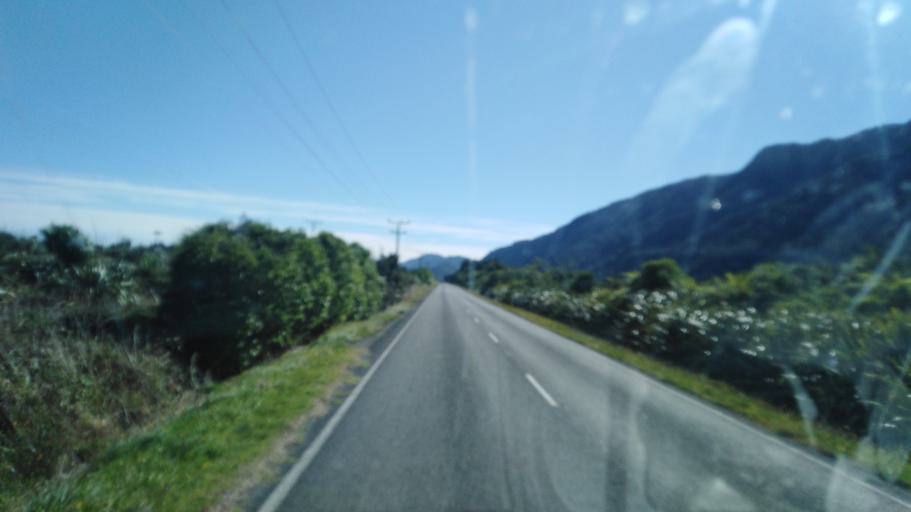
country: NZ
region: West Coast
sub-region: Buller District
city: Westport
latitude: -41.6604
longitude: 171.8178
